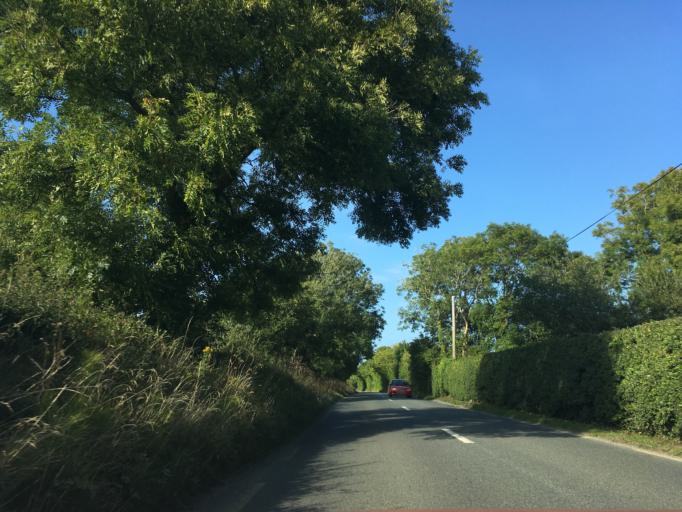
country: IE
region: Leinster
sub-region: Loch Garman
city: Loch Garman
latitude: 52.2770
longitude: -6.4699
